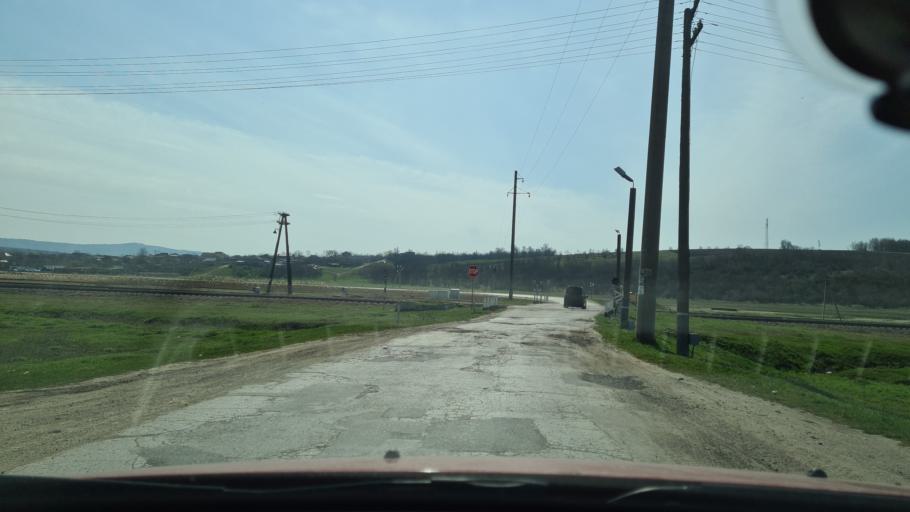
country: MD
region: Ungheni
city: Ungheni
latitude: 47.3211
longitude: 27.8879
